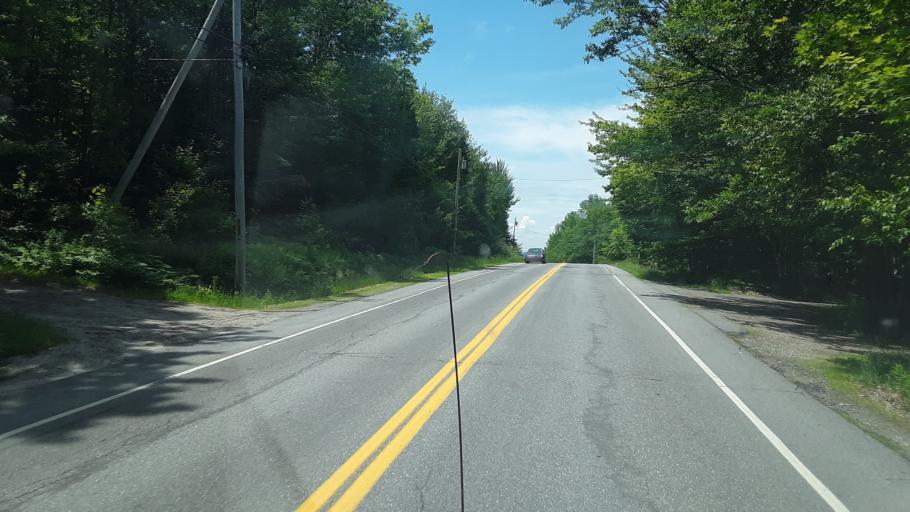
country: US
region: Maine
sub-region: Hancock County
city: Bucksport
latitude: 44.5669
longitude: -68.8329
